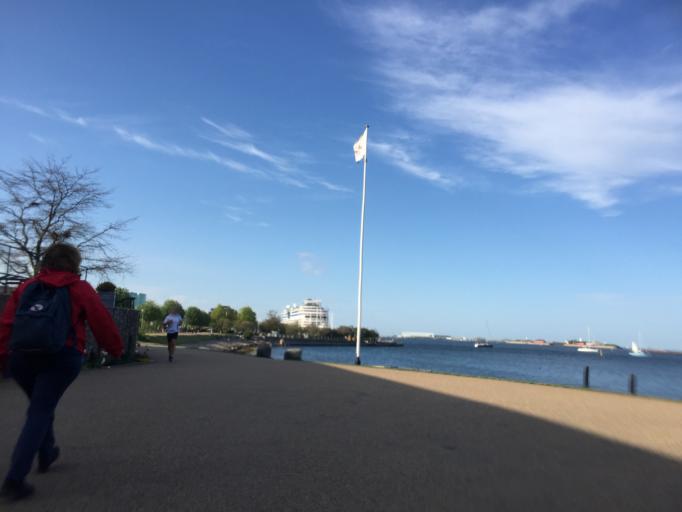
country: DK
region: Capital Region
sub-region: Kobenhavn
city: Christianshavn
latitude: 55.6912
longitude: 12.5988
